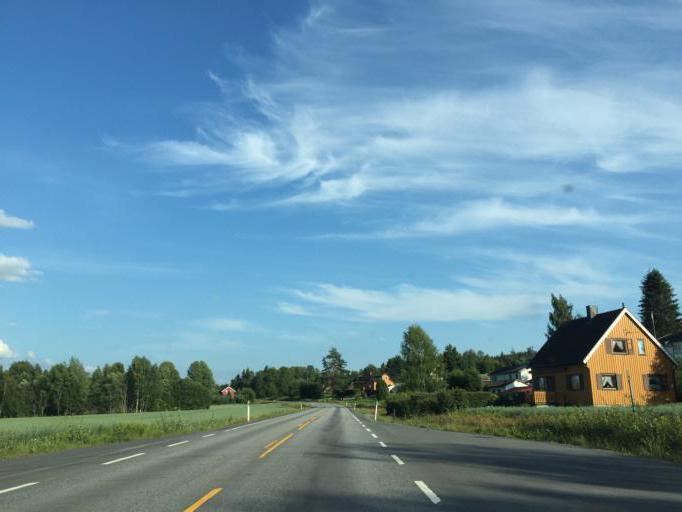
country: NO
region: Hedmark
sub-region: Sor-Odal
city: Skarnes
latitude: 60.2410
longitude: 11.7146
